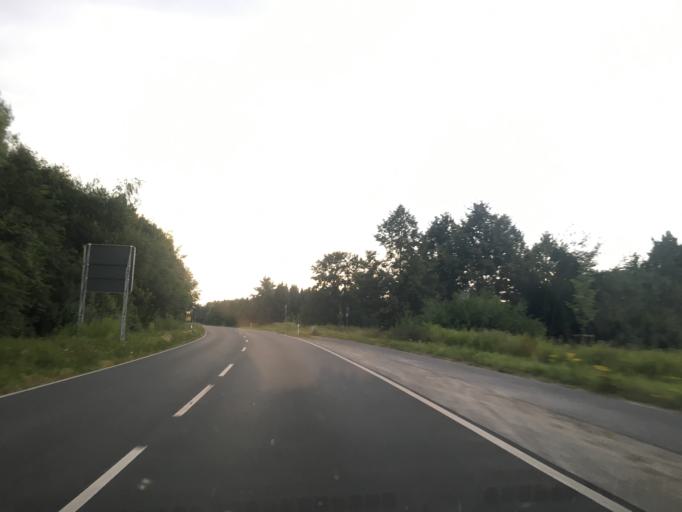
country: DE
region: North Rhine-Westphalia
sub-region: Regierungsbezirk Munster
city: Telgte
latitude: 51.9342
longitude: 7.7164
